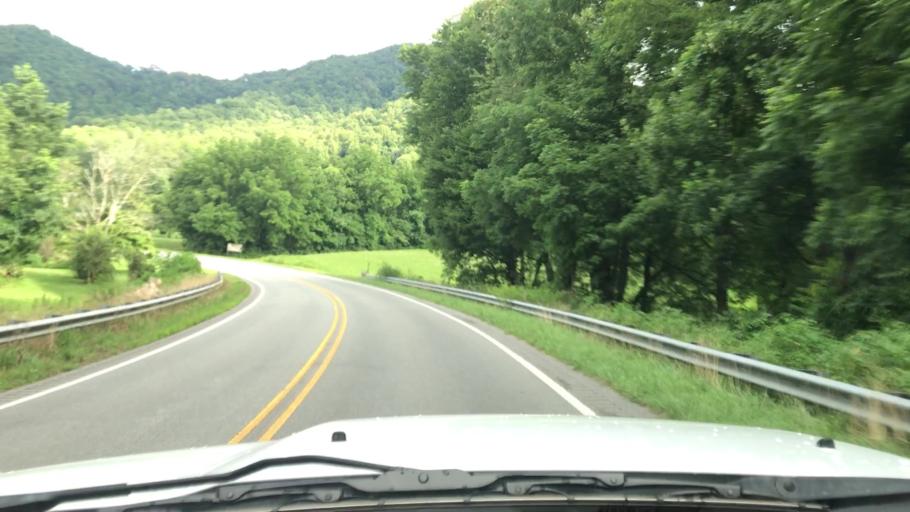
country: US
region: North Carolina
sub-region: Graham County
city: Robbinsville
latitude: 35.2710
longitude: -83.7541
